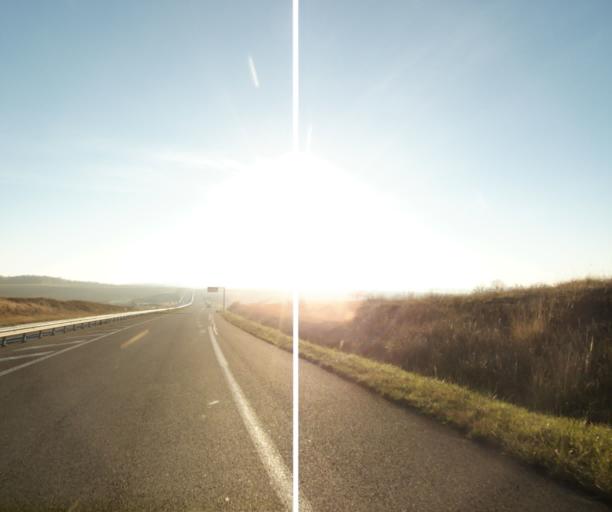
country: FR
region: Poitou-Charentes
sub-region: Departement de la Charente-Maritime
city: Cherac
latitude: 45.7083
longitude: -0.4852
